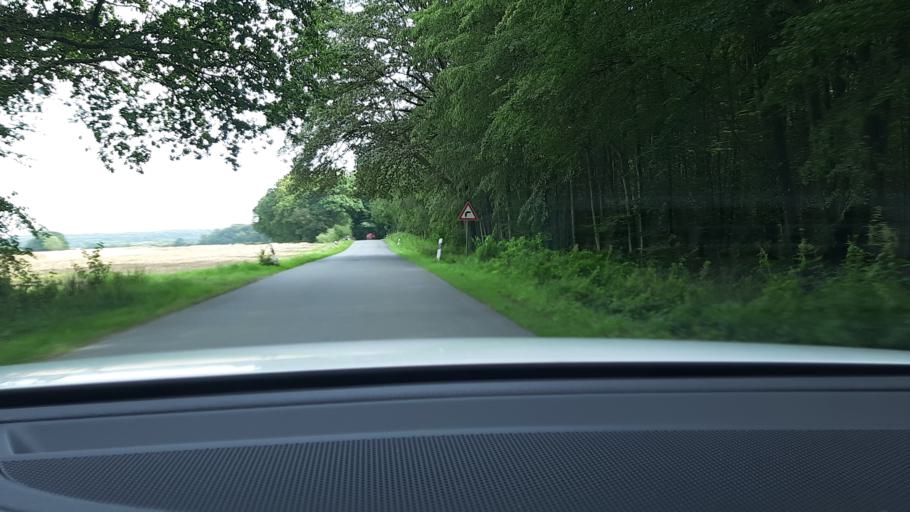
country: DE
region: Schleswig-Holstein
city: Rehhorst
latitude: 53.8547
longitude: 10.4712
